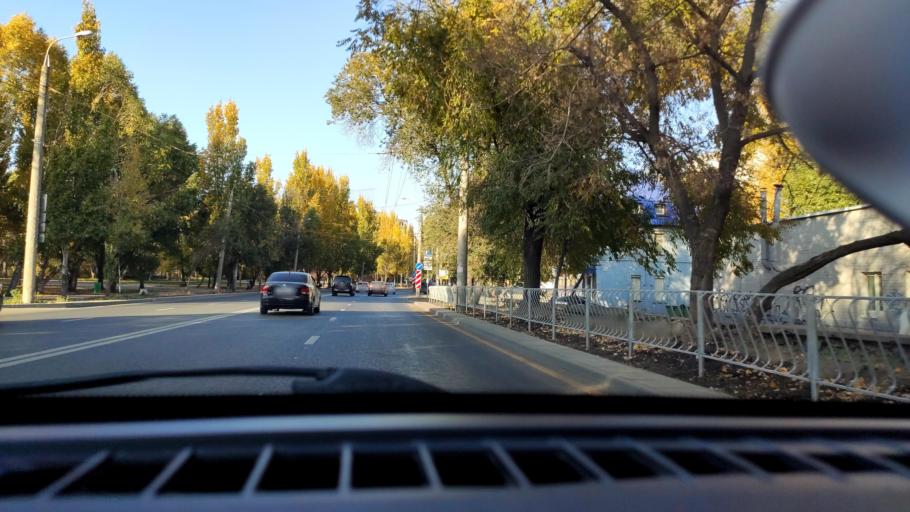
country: RU
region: Samara
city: Samara
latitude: 53.2404
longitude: 50.2277
